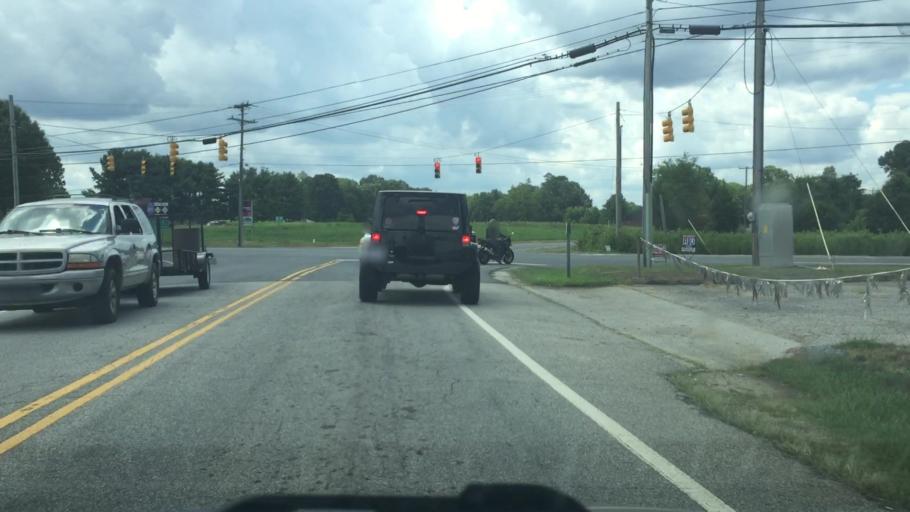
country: US
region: North Carolina
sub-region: Rowan County
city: Enochville
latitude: 35.5717
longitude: -80.6544
